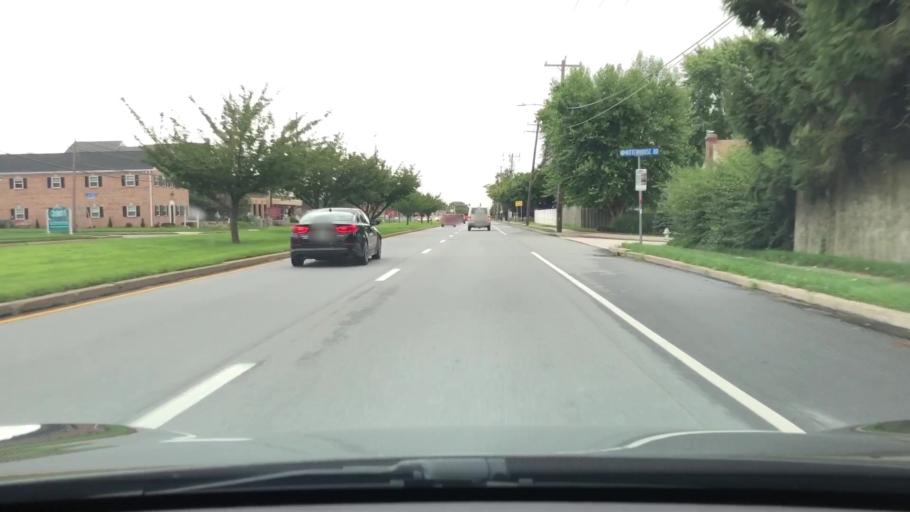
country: US
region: Pennsylvania
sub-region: Delaware County
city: Broomall
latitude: 39.9827
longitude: -75.3680
